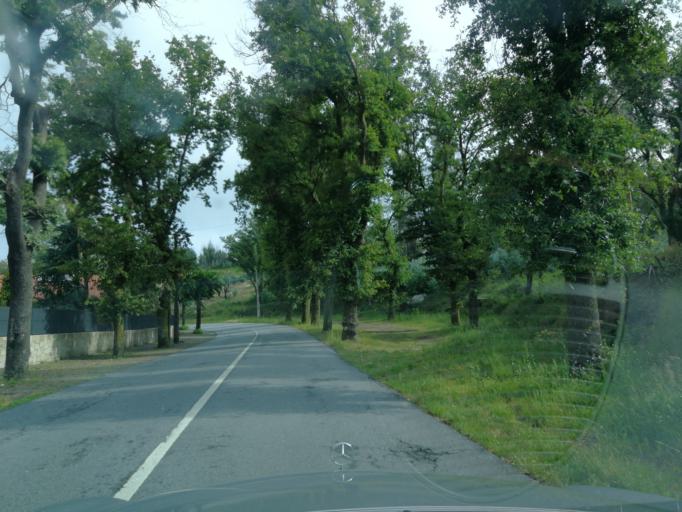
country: PT
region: Braga
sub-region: Braga
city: Braga
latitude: 41.5462
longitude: -8.3741
